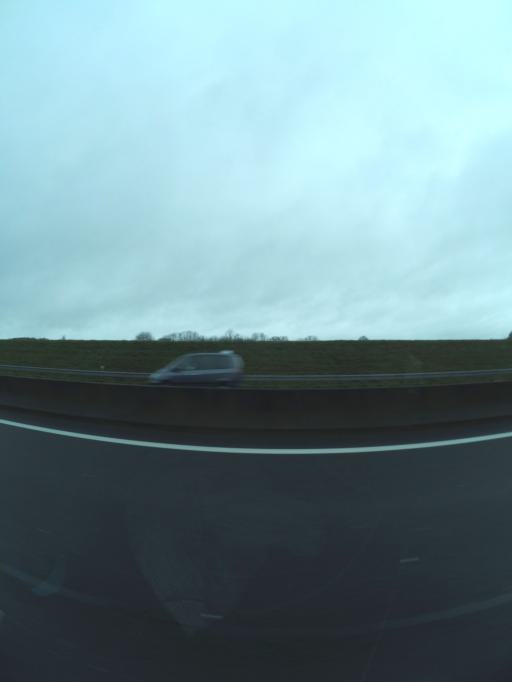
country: FR
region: Pays de la Loire
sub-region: Departement de Maine-et-Loire
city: Saint-Lambert-la-Potherie
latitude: 47.4777
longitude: -0.6715
